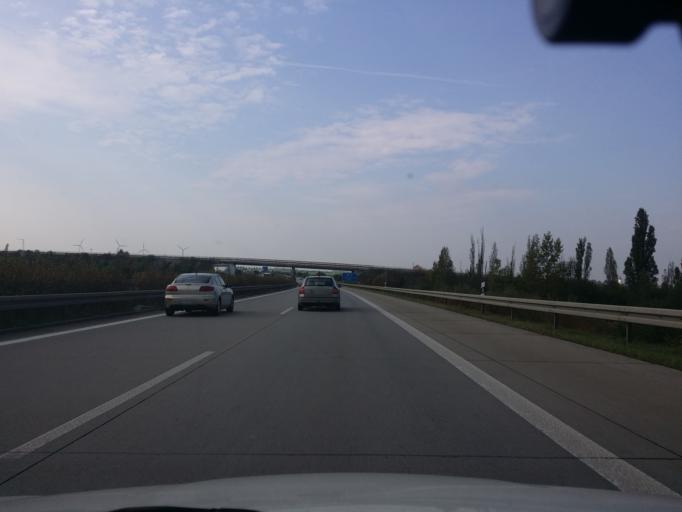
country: DE
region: Saxony
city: Zwenkau
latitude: 51.2592
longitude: 12.2907
